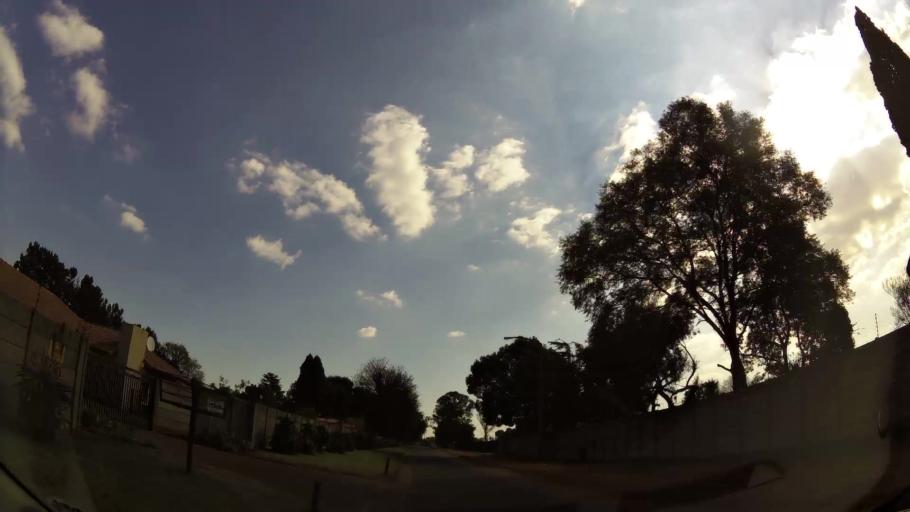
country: ZA
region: Gauteng
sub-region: Ekurhuleni Metropolitan Municipality
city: Benoni
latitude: -26.1204
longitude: 28.3479
